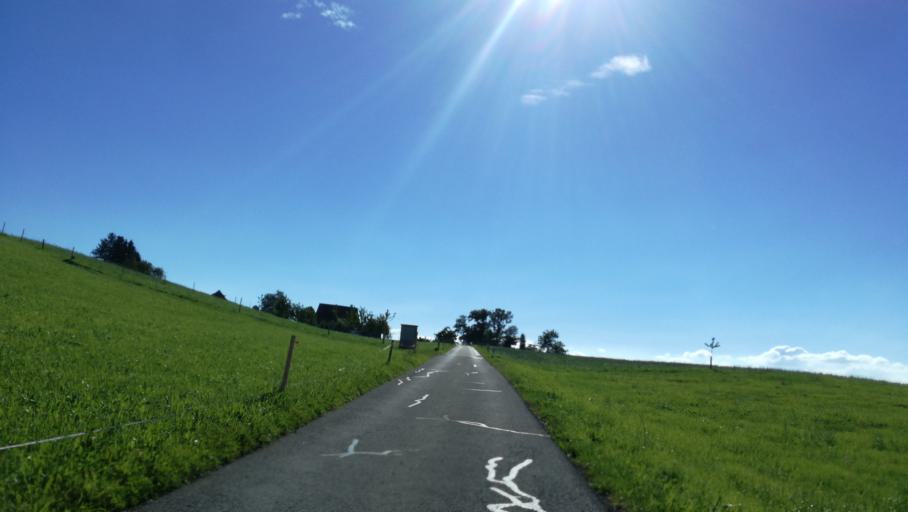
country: CH
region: Zug
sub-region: Zug
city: Zug
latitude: 47.1625
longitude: 8.5407
